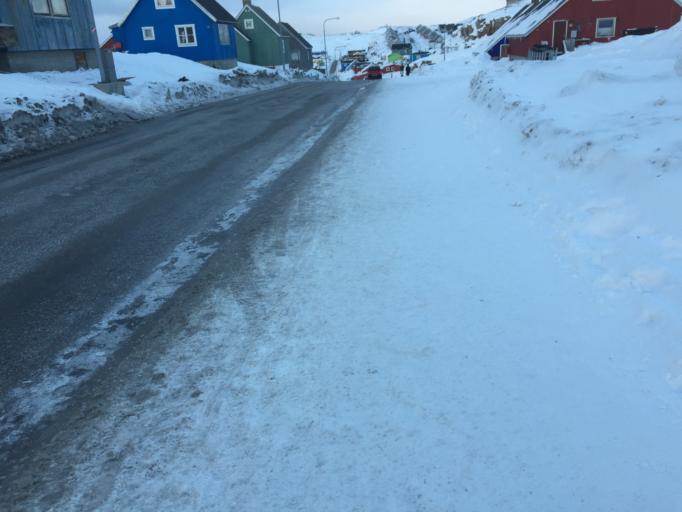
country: GL
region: Qaasuitsup
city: Aasiaat
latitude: 68.7097
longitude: -52.8583
